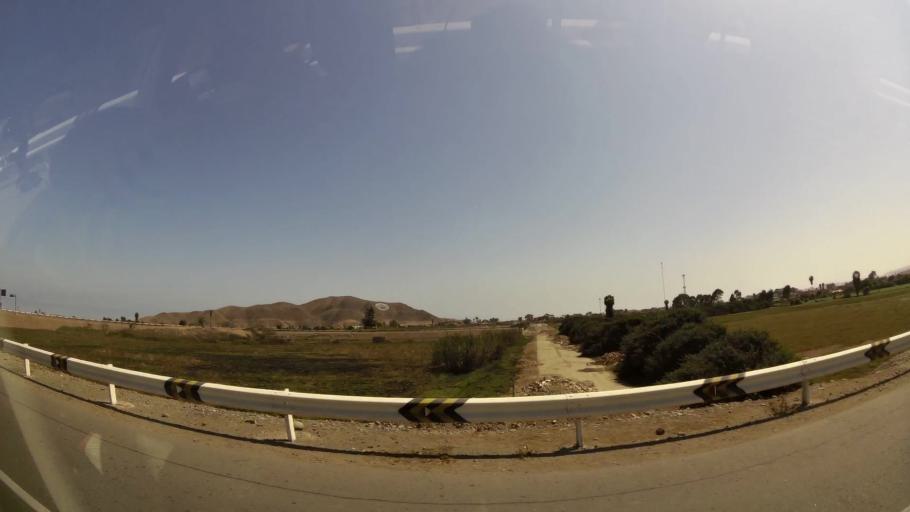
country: PE
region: Lima
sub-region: Provincia de Canete
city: San Vicente de Canete
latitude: -13.0309
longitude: -76.4730
